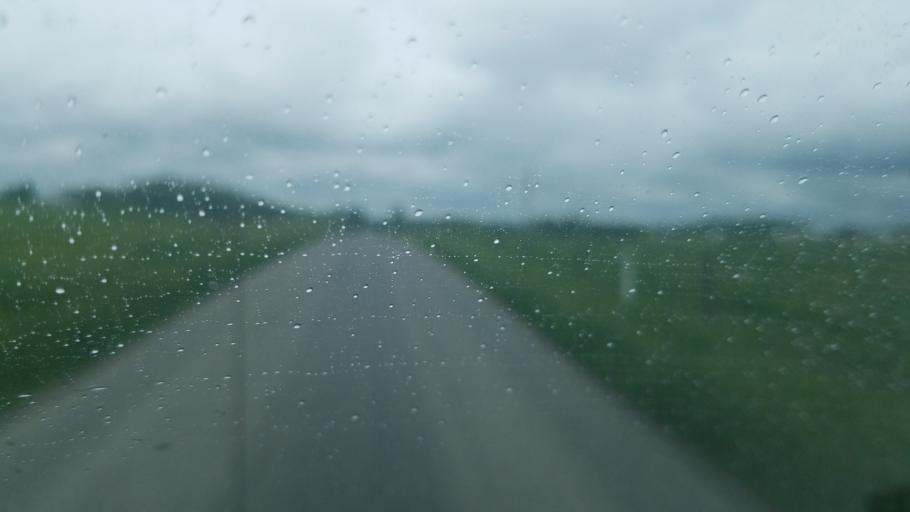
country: US
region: Ohio
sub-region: Wayne County
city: Apple Creek
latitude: 40.7346
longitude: -81.7849
